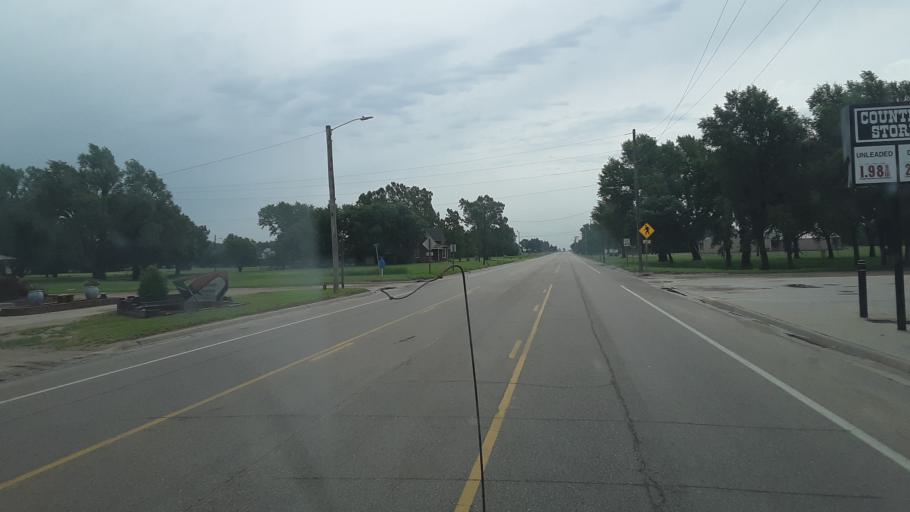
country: US
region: Kansas
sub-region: Stafford County
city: Saint John
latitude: 37.9566
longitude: -98.9671
